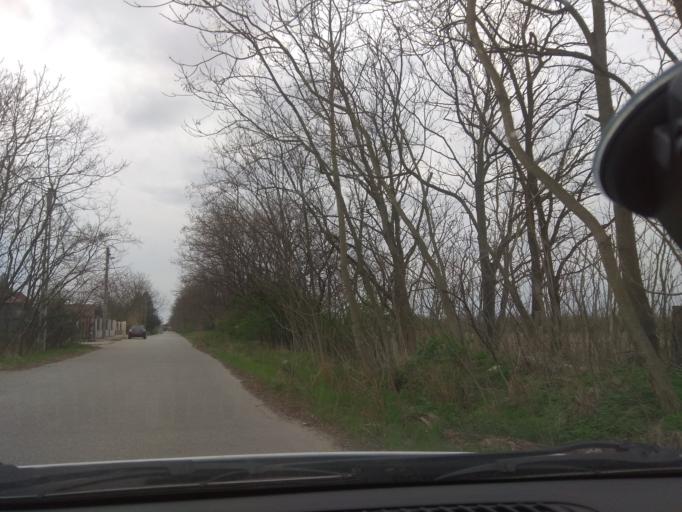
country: HU
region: Pest
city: Halasztelek
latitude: 47.3739
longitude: 19.0145
